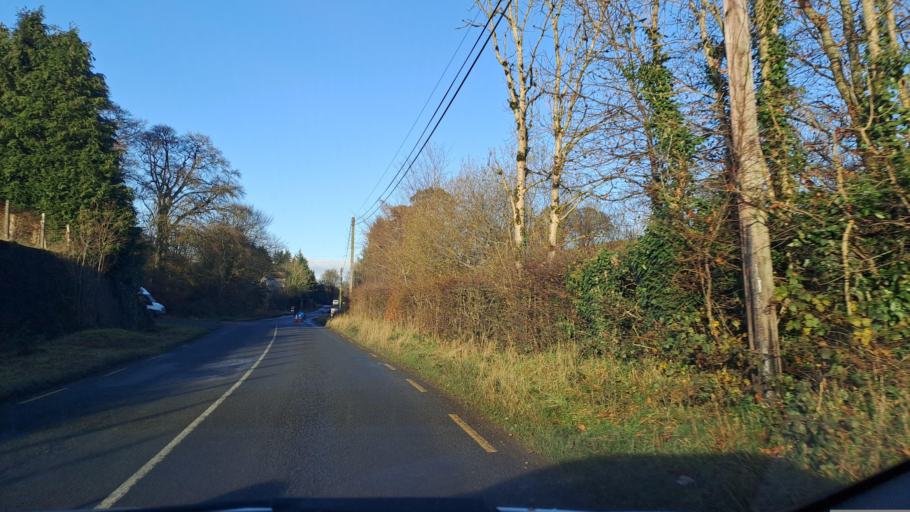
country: IE
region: Ulster
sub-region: An Cabhan
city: Bailieborough
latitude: 53.8999
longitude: -6.9666
